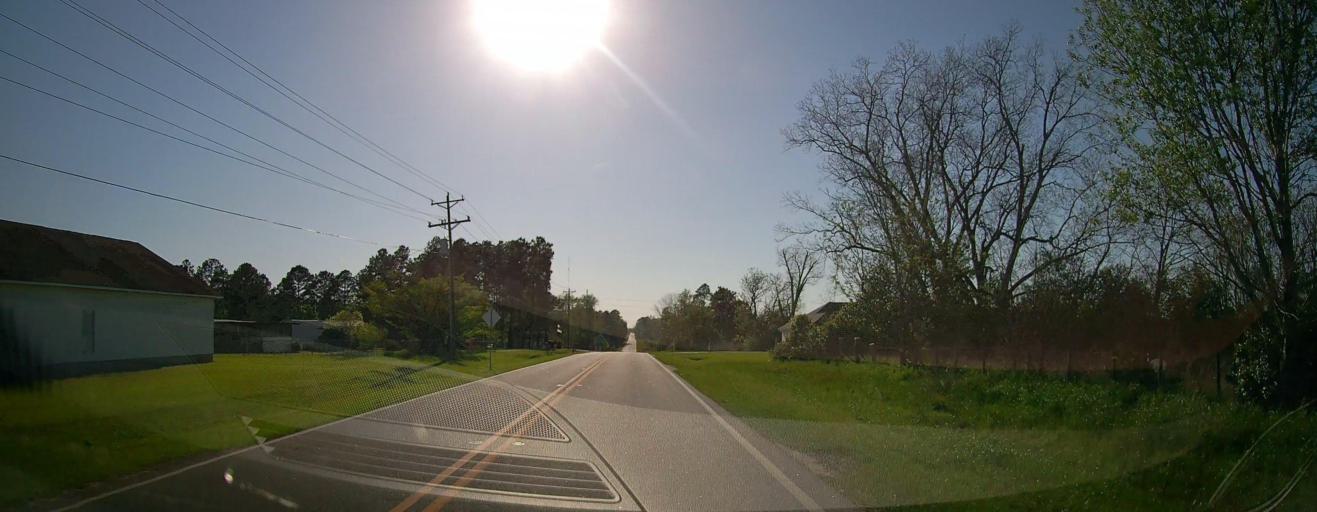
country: US
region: Georgia
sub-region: Ben Hill County
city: Fitzgerald
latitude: 31.7431
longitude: -83.2351
